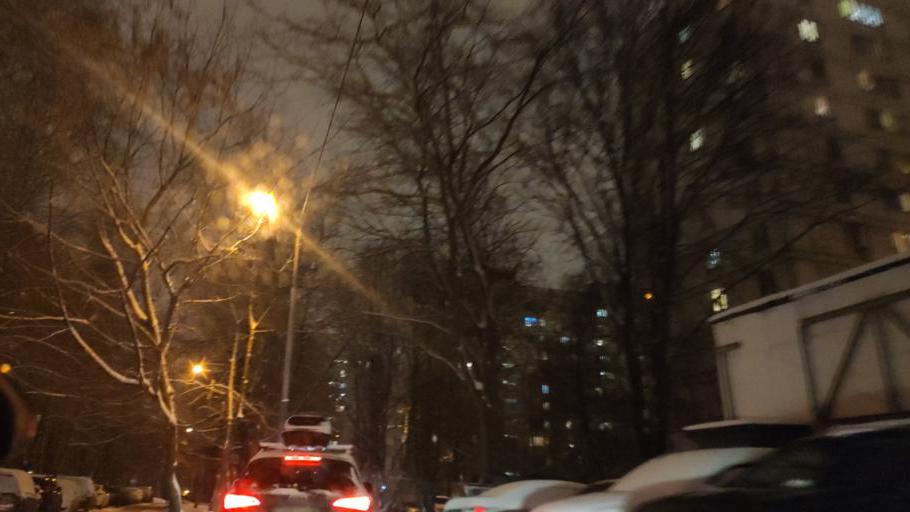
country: RU
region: Moscow
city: Tyoply Stan
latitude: 55.6222
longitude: 37.4892
